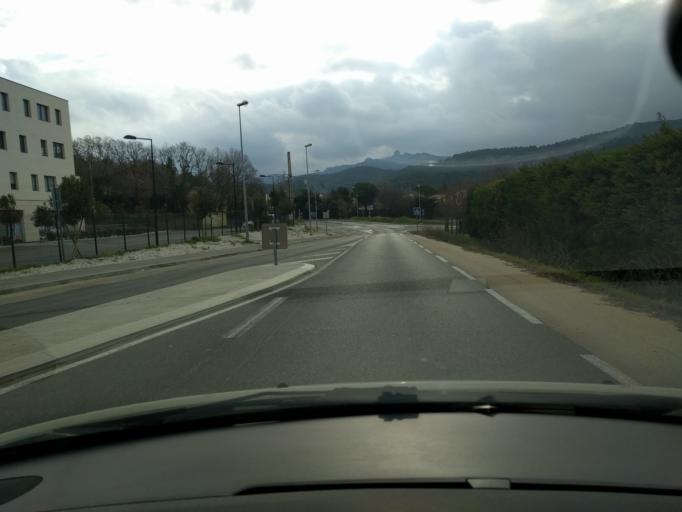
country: FR
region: Provence-Alpes-Cote d'Azur
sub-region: Departement des Bouches-du-Rhone
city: Simiane-Collongue
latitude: 43.4347
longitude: 5.4278
